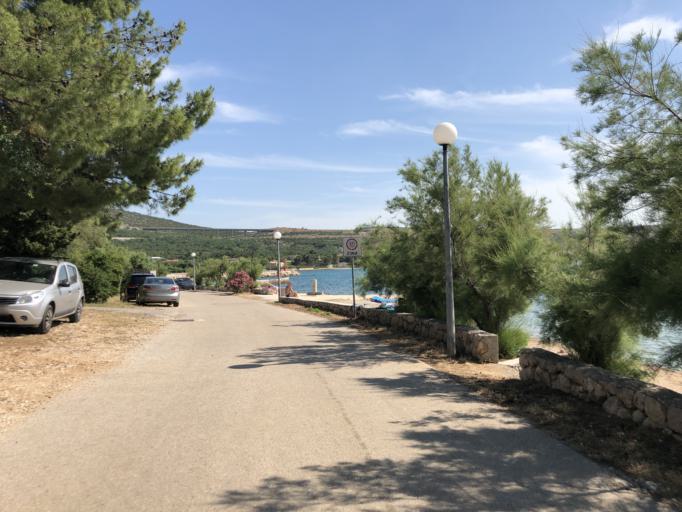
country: HR
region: Zadarska
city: Posedarje
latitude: 44.2514
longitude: 15.5368
